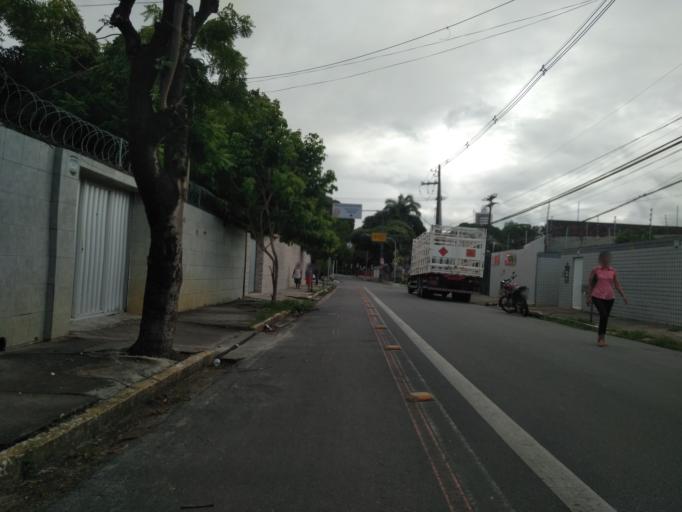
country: BR
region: Pernambuco
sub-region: Recife
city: Recife
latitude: -8.0317
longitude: -34.8848
